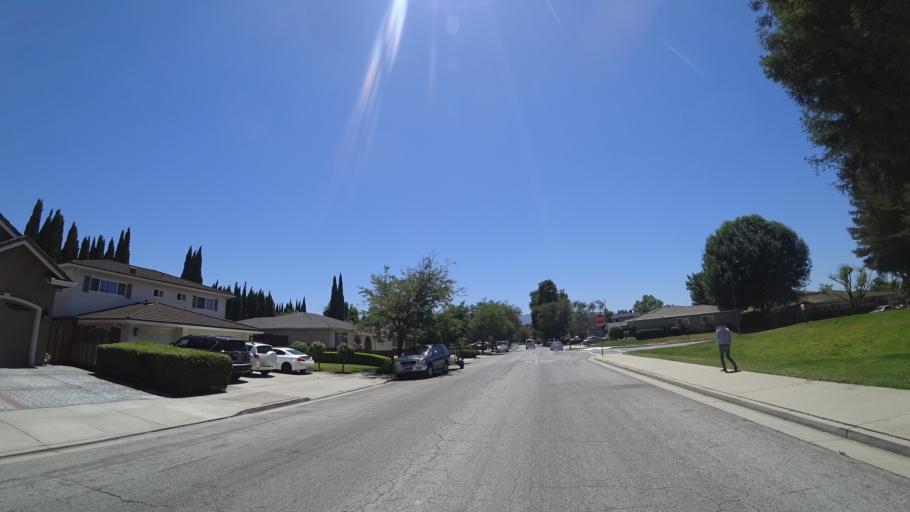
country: US
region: California
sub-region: Santa Clara County
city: Seven Trees
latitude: 37.2620
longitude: -121.8496
